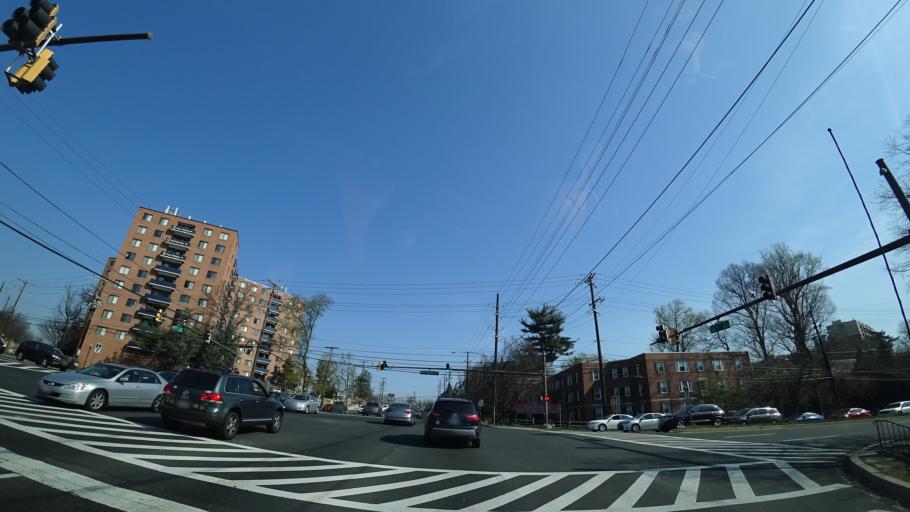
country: US
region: Maryland
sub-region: Montgomery County
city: Silver Spring
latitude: 38.9943
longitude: -77.0362
